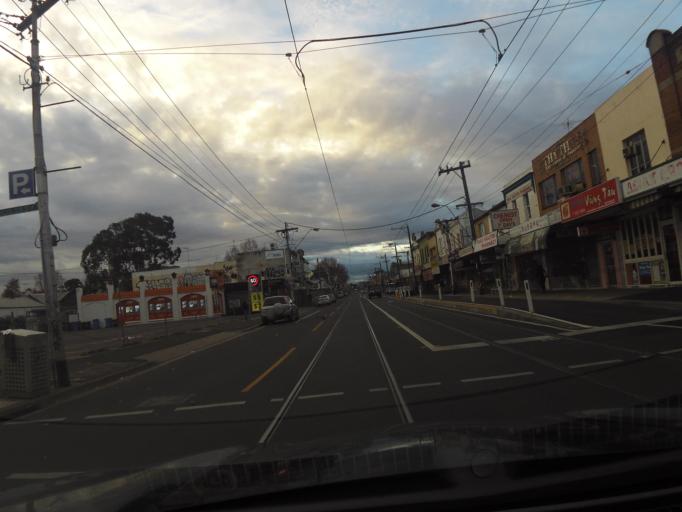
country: AU
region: Victoria
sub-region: Yarra
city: Richmond
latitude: -37.8100
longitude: 144.9960
